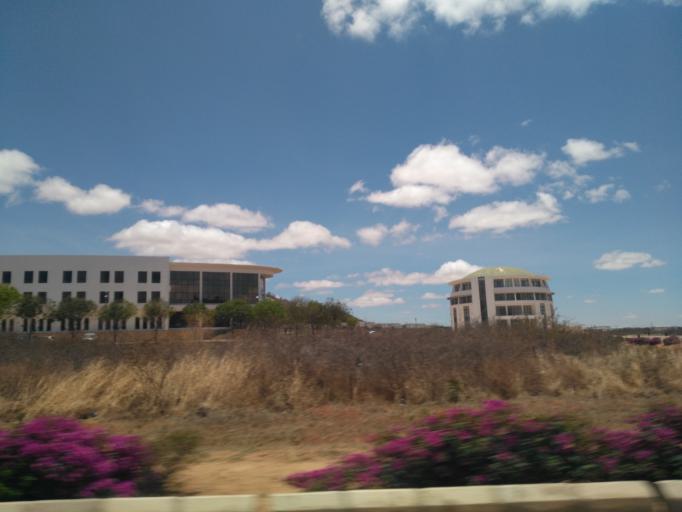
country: TZ
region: Dodoma
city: Kisasa
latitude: -6.2165
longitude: 35.8100
